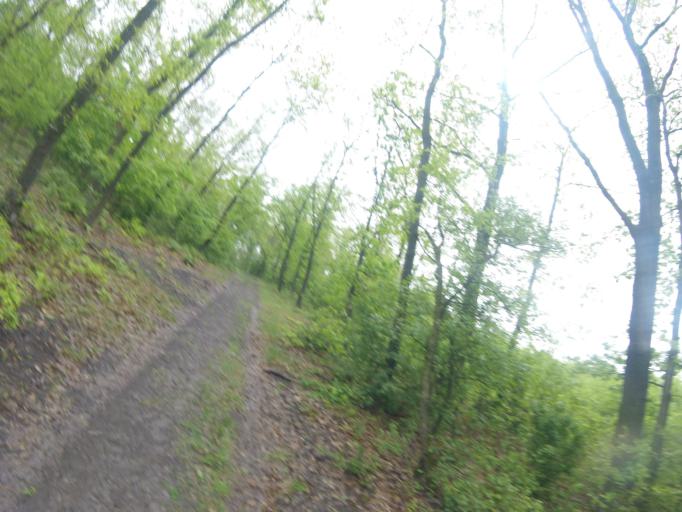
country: HU
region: Nograd
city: Matraverebely
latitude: 47.9963
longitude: 19.7574
